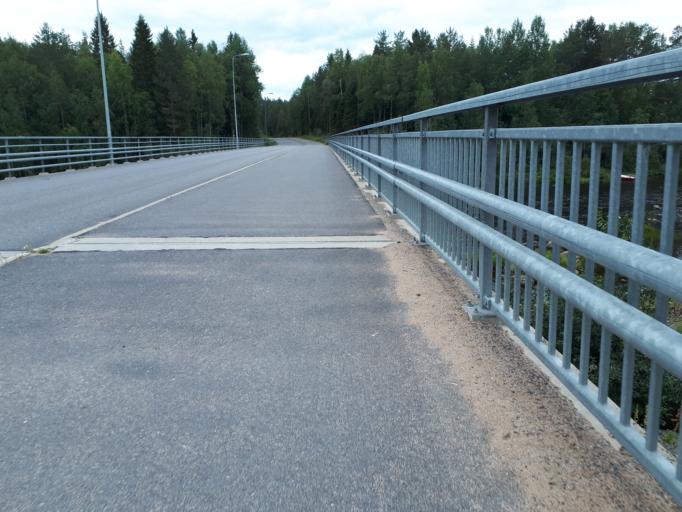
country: FI
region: Northern Ostrobothnia
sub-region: Oulunkaari
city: Ii
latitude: 65.3226
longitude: 25.4101
